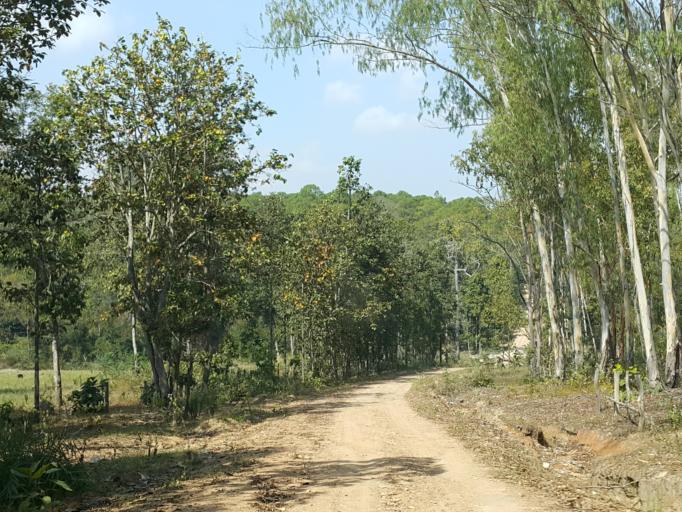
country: TH
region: Chiang Mai
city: Hot
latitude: 18.1485
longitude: 98.4316
